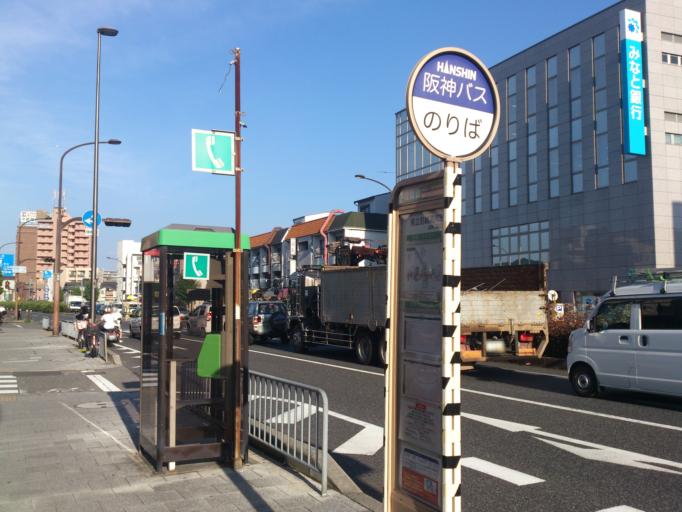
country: JP
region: Hyogo
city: Amagasaki
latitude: 34.7197
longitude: 135.4236
